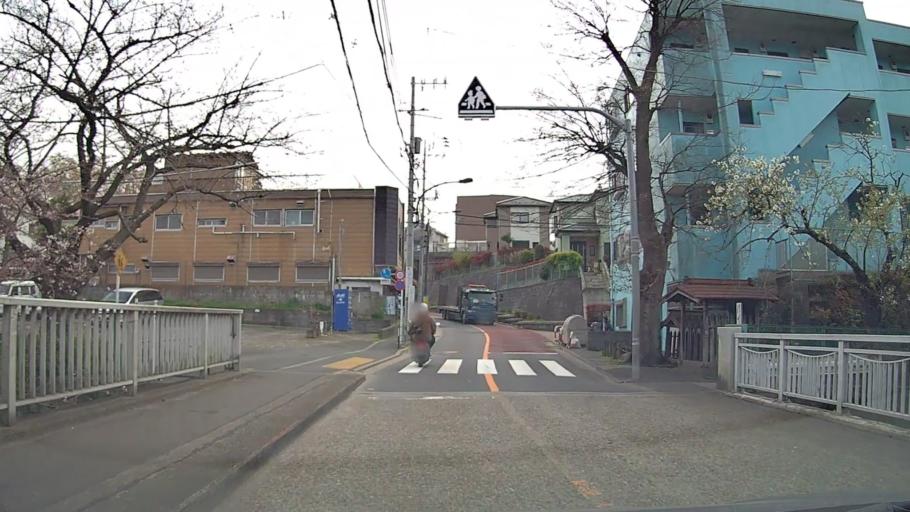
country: JP
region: Saitama
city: Wako
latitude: 35.7655
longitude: 139.6067
